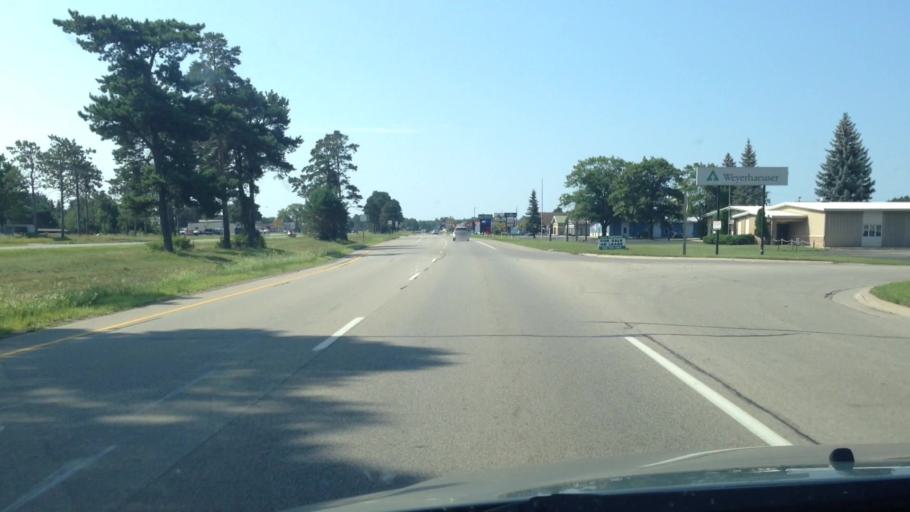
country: US
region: Michigan
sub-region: Delta County
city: Escanaba
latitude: 45.7829
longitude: -87.0833
